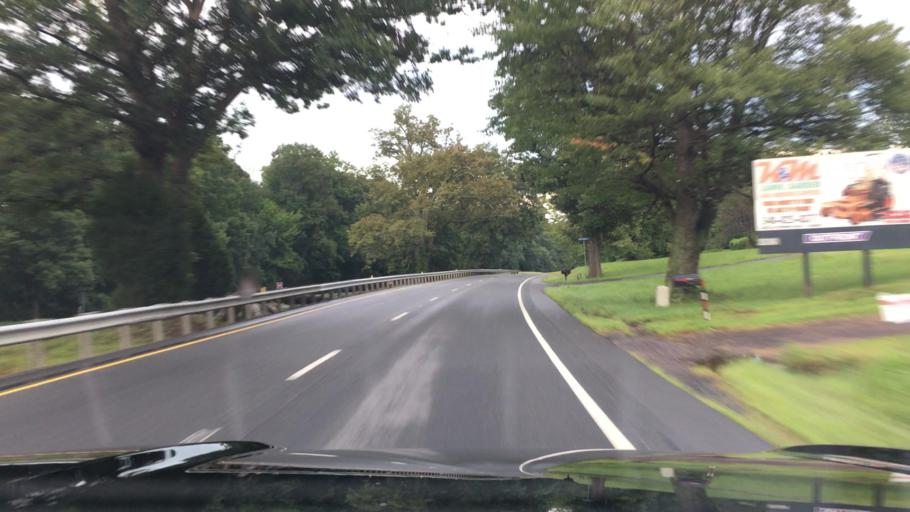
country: US
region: Virginia
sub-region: Culpeper County
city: Merrimac
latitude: 38.4532
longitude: -78.0770
